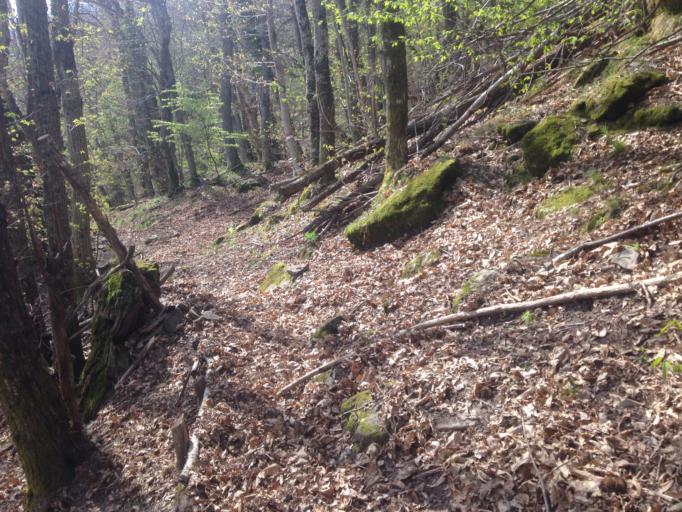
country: IT
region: Emilia-Romagna
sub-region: Provincia di Bologna
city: Lizzano in Belvedere
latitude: 44.1535
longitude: 10.8900
